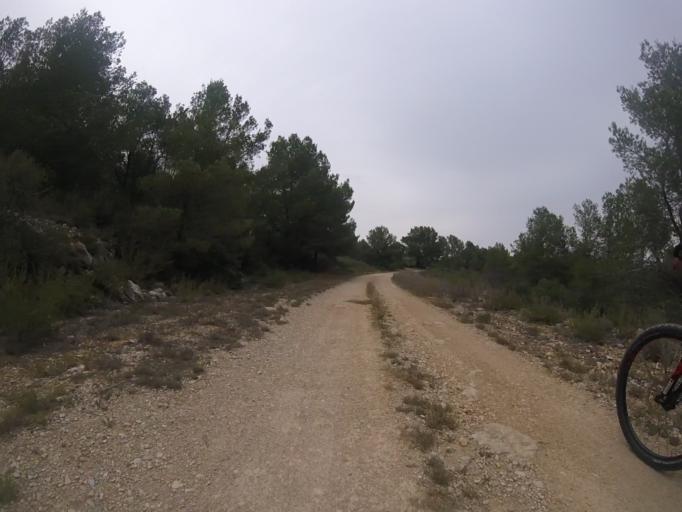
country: ES
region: Valencia
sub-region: Provincia de Castello
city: Alcoceber
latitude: 40.2815
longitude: 0.2832
